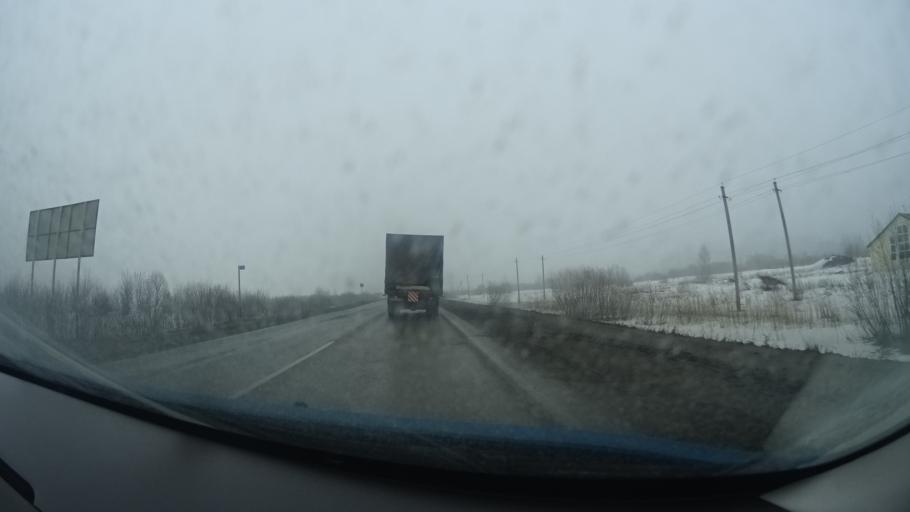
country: RU
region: Perm
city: Kuyeda
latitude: 56.4428
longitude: 55.5797
